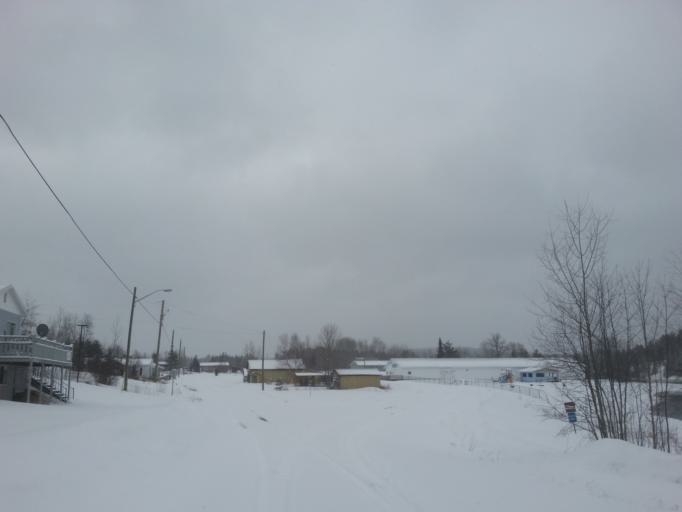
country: CA
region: Ontario
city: Kirkland Lake
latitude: 47.9373
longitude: -80.6510
